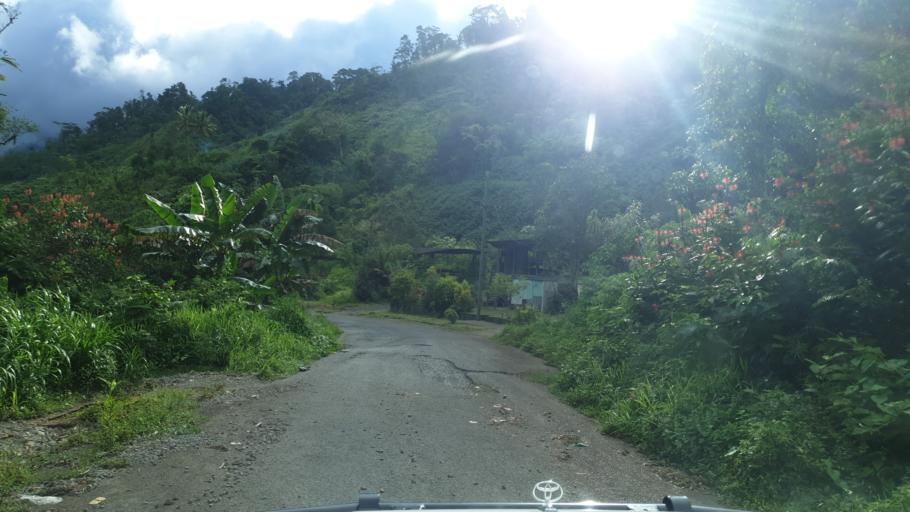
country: PG
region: Bougainville
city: Panguna
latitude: -6.2995
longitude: 155.4938
